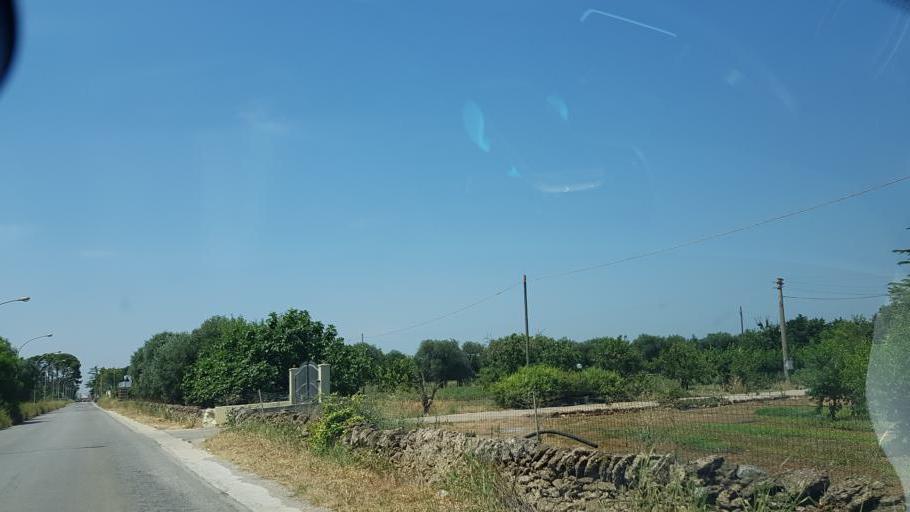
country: IT
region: Apulia
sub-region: Provincia di Brindisi
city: Mesagne
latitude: 40.5479
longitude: 17.8191
